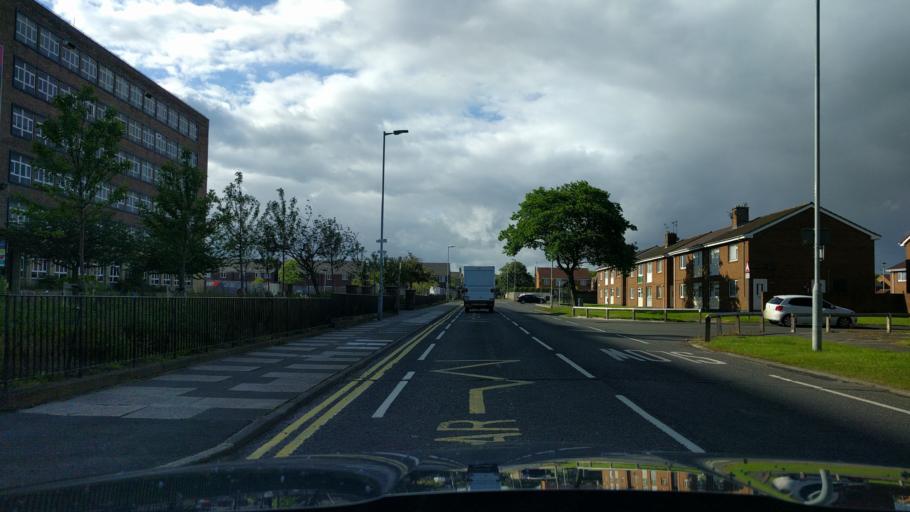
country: GB
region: England
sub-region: Northumberland
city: Ashington
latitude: 55.1731
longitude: -1.5561
